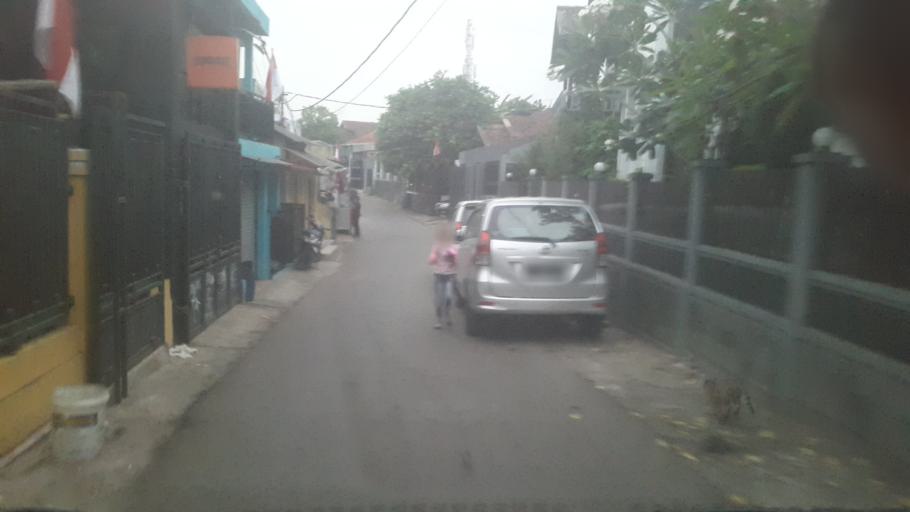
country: ID
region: West Java
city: Pelabuhanratu
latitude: -6.9898
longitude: 106.5522
